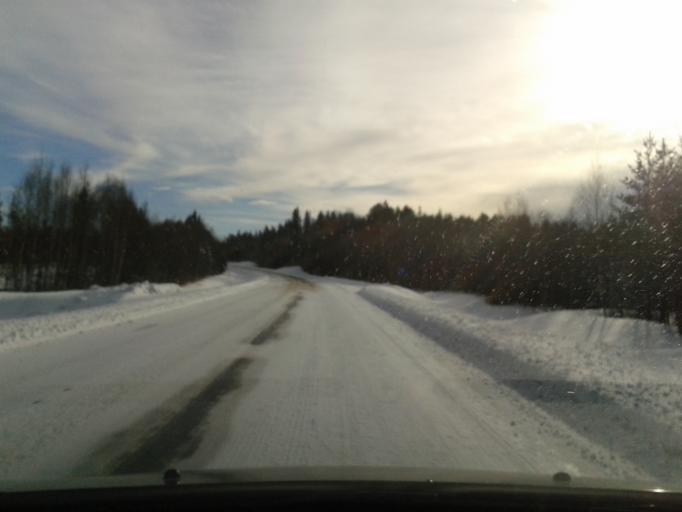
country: SE
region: Vaesterbotten
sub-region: Vilhelmina Kommun
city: Vilhelmina
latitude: 64.5409
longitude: 16.7473
